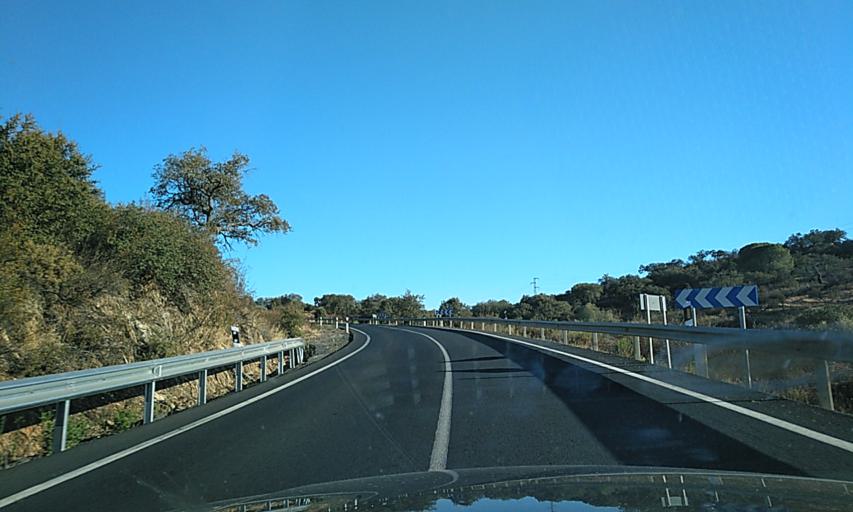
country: ES
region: Andalusia
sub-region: Provincia de Huelva
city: Alosno
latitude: 37.5233
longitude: -7.1356
